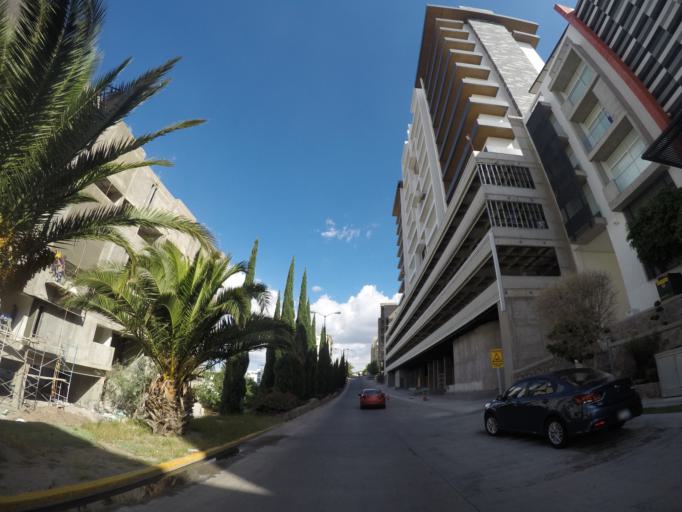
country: MX
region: San Luis Potosi
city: Escalerillas
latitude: 22.1231
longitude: -101.0342
